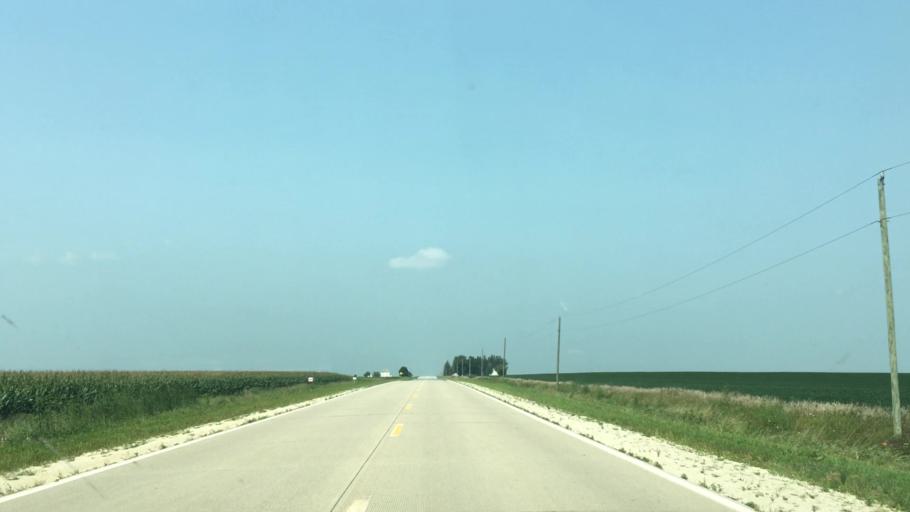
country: US
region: Iowa
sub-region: Fayette County
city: Oelwein
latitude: 42.7047
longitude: -91.8048
